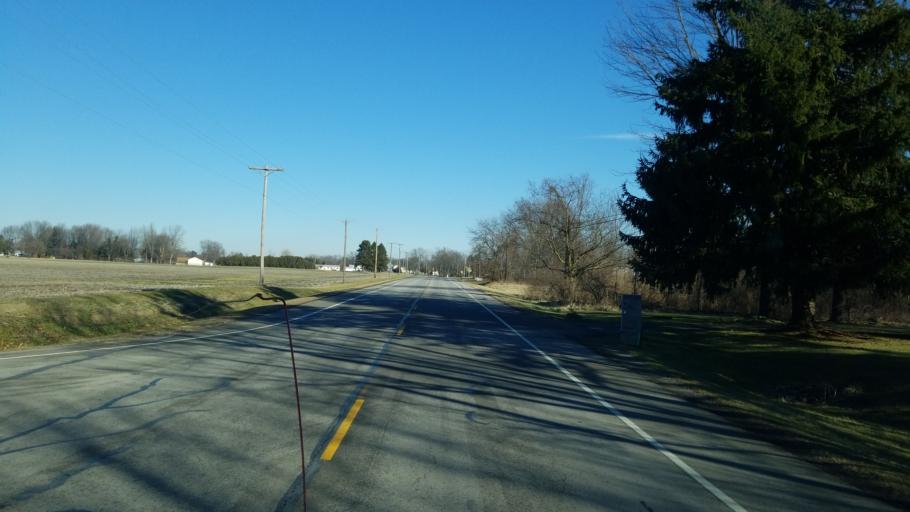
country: US
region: Ohio
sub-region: Lucas County
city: Whitehouse
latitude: 41.4507
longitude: -83.7925
